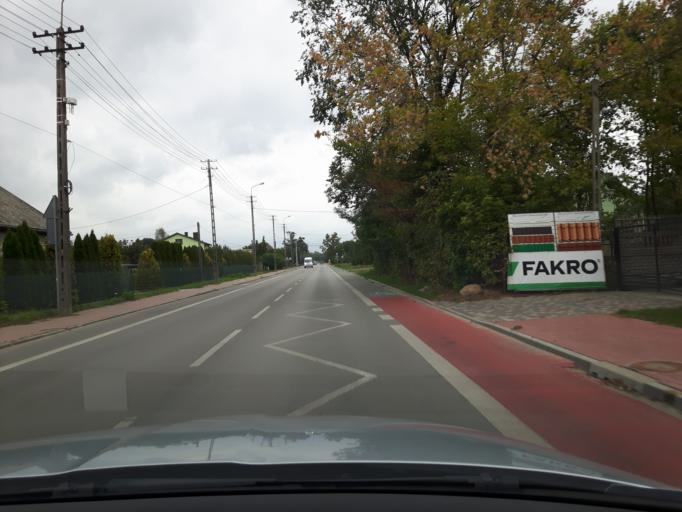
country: PL
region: Masovian Voivodeship
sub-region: Powiat wolominski
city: Kobylka
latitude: 52.3156
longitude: 21.1875
